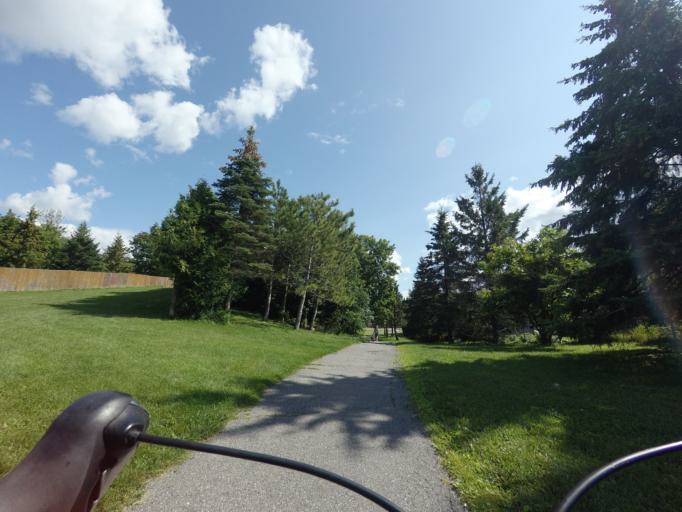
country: CA
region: Ontario
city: Bells Corners
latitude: 45.2928
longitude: -75.8630
